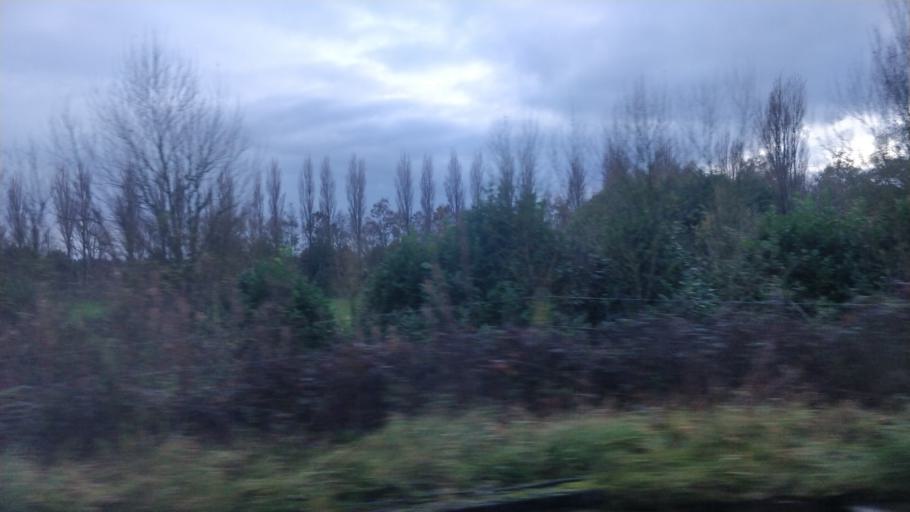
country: GB
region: England
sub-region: Lancashire
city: Banks
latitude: 53.6232
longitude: -2.9126
